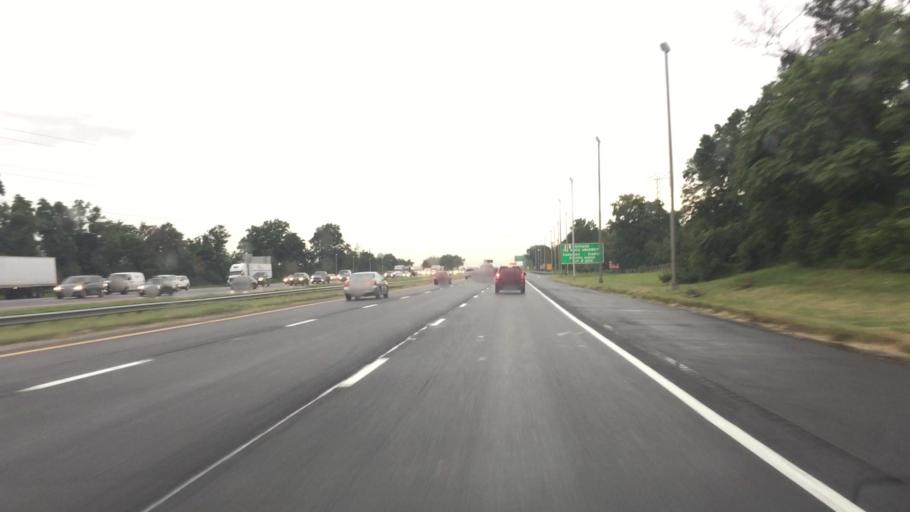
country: US
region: New Jersey
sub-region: Middlesex County
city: Society Hill
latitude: 40.5562
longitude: -74.4535
